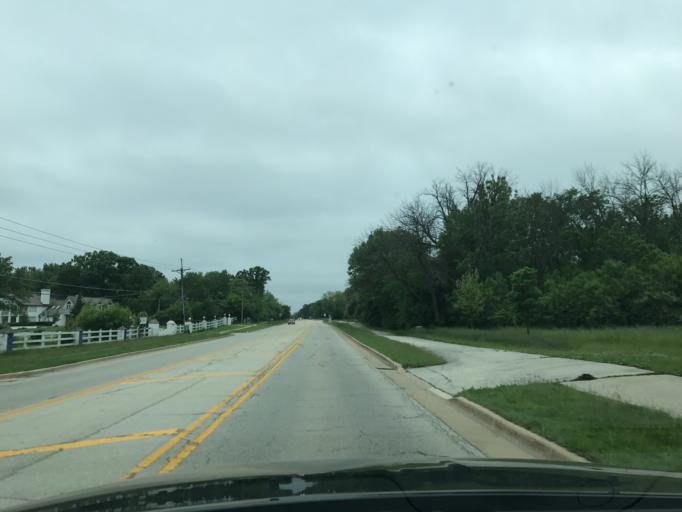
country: US
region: Illinois
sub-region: DuPage County
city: Woodridge
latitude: 41.7572
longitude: -88.0872
